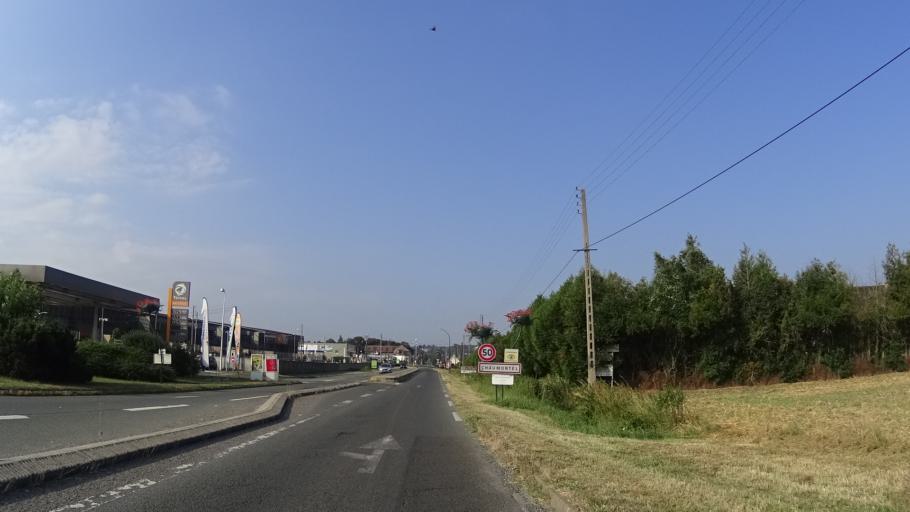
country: FR
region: Ile-de-France
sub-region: Departement du Val-d'Oise
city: Chaumontel
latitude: 49.1285
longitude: 2.4309
